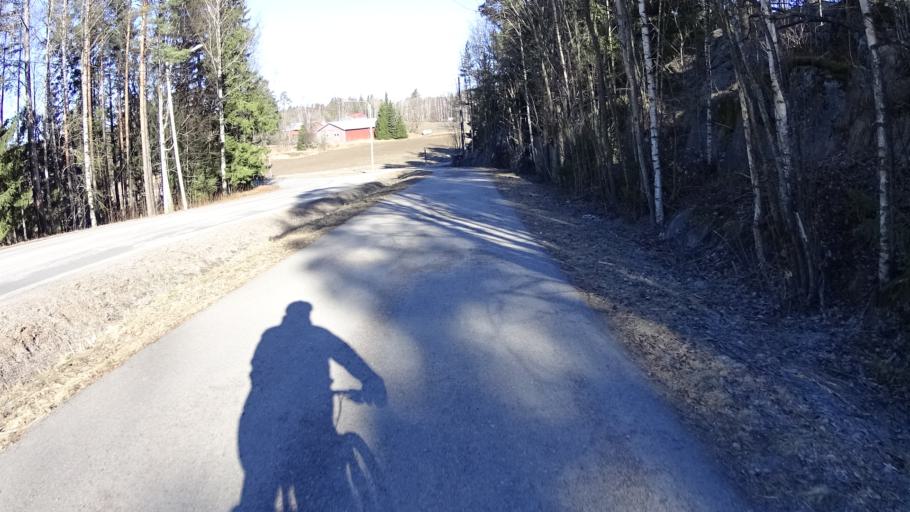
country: FI
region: Uusimaa
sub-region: Helsinki
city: Espoo
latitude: 60.2290
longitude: 24.6651
